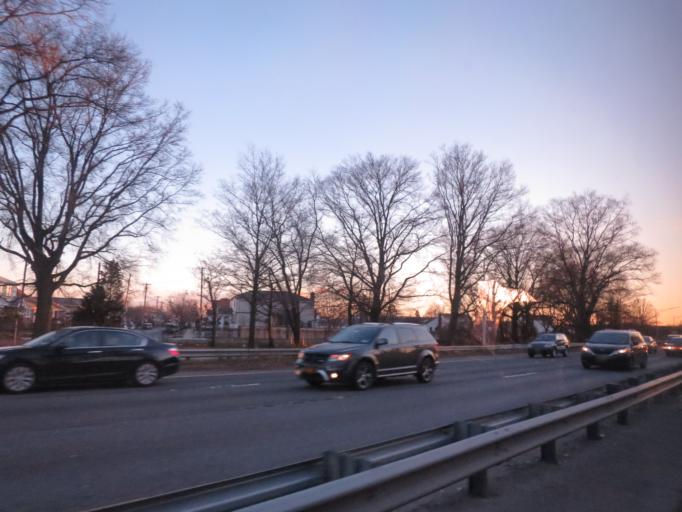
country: US
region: New York
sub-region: Queens County
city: Borough of Queens
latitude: 40.6607
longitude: -73.8524
